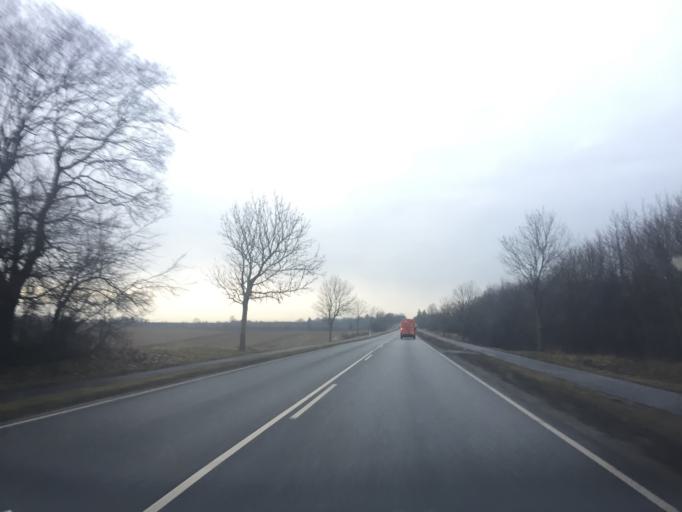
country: DK
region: Zealand
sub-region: Solrod Kommune
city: Solrod Strand
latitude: 55.5770
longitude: 12.2353
